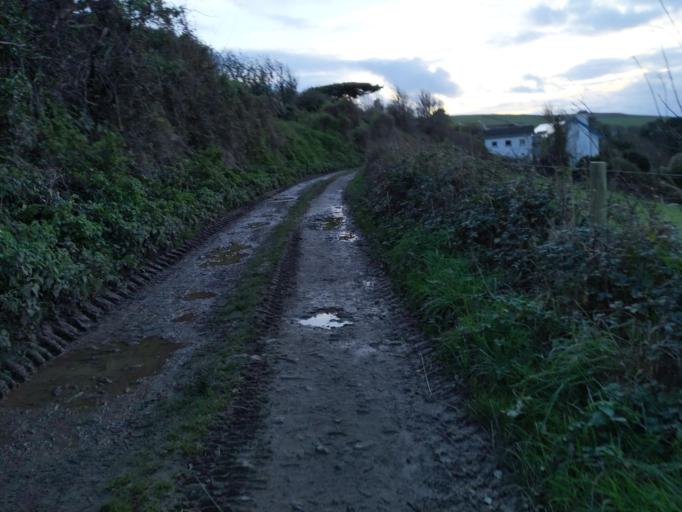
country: GB
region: England
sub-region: Devon
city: Modbury
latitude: 50.2805
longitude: -3.8650
